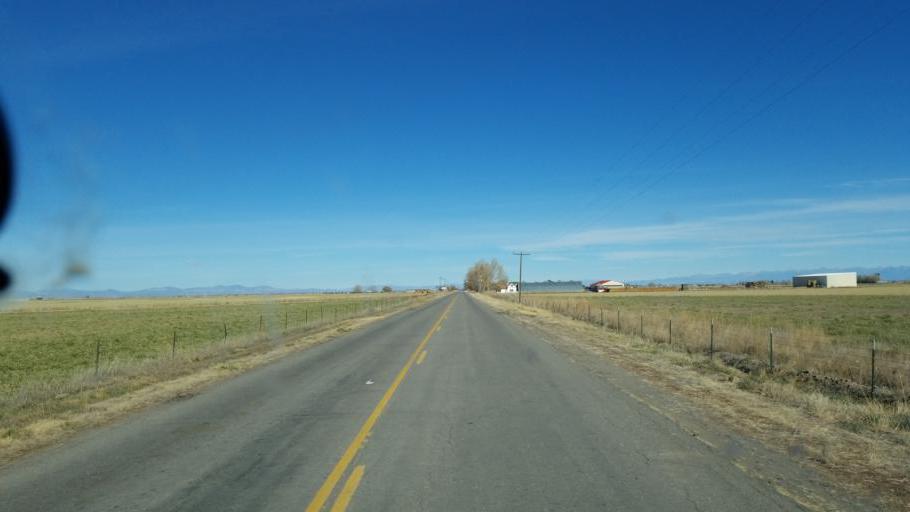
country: US
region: Colorado
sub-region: Rio Grande County
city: Monte Vista
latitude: 37.4303
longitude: -106.0942
